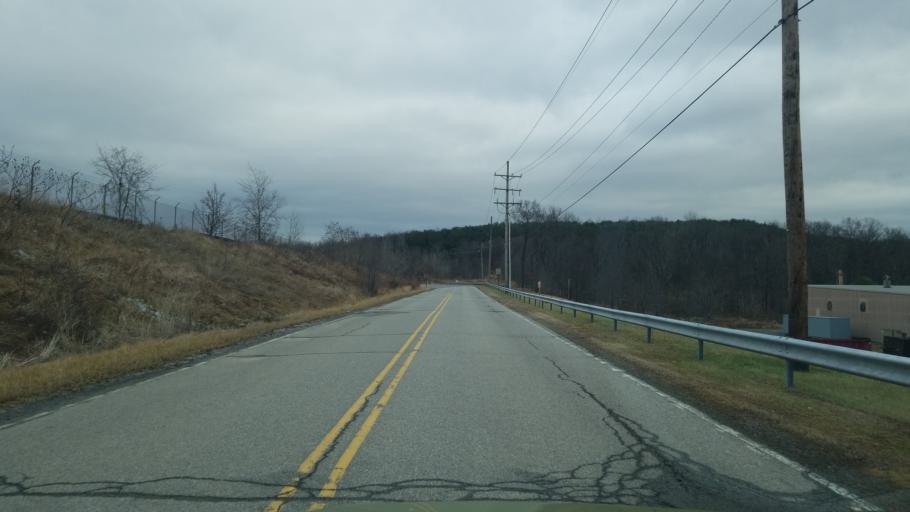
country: US
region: Pennsylvania
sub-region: Clearfield County
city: Clearfield
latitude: 41.0276
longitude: -78.3918
